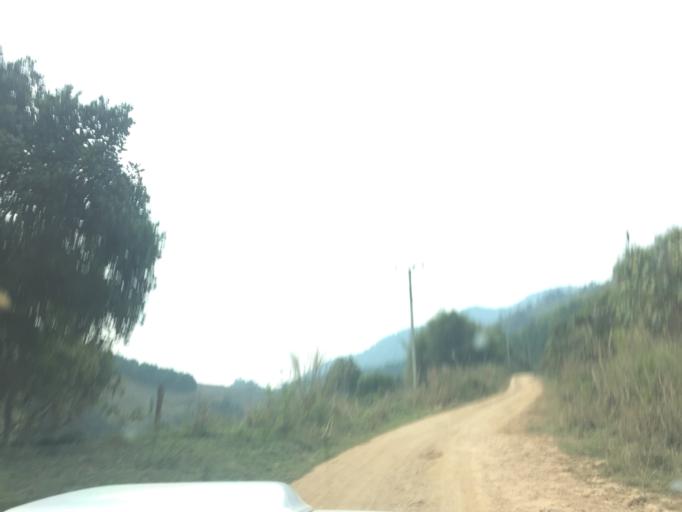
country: TH
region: Nan
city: Song Khwae
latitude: 19.7397
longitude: 100.7149
